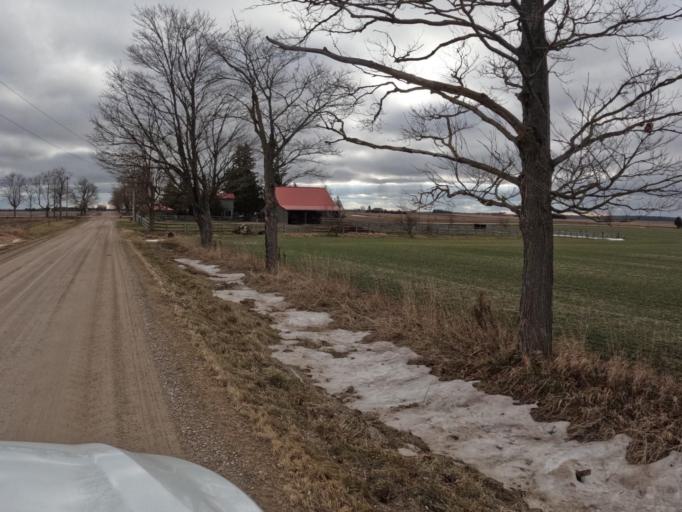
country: CA
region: Ontario
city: Shelburne
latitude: 43.8820
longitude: -80.4044
